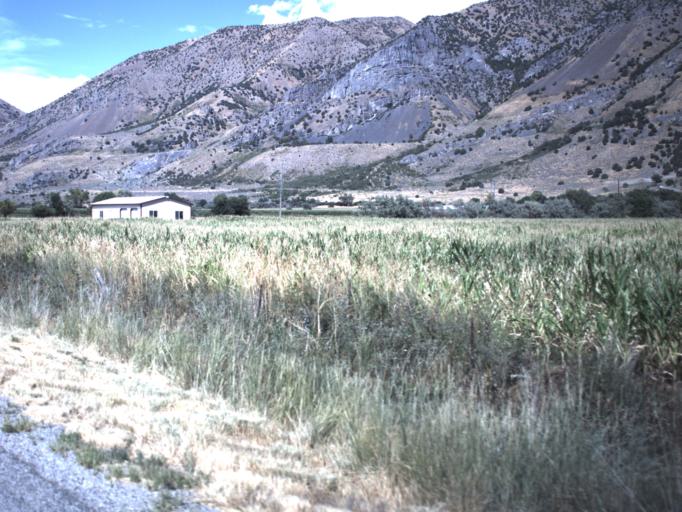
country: US
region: Utah
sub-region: Box Elder County
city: Honeyville
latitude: 41.6848
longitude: -112.0899
